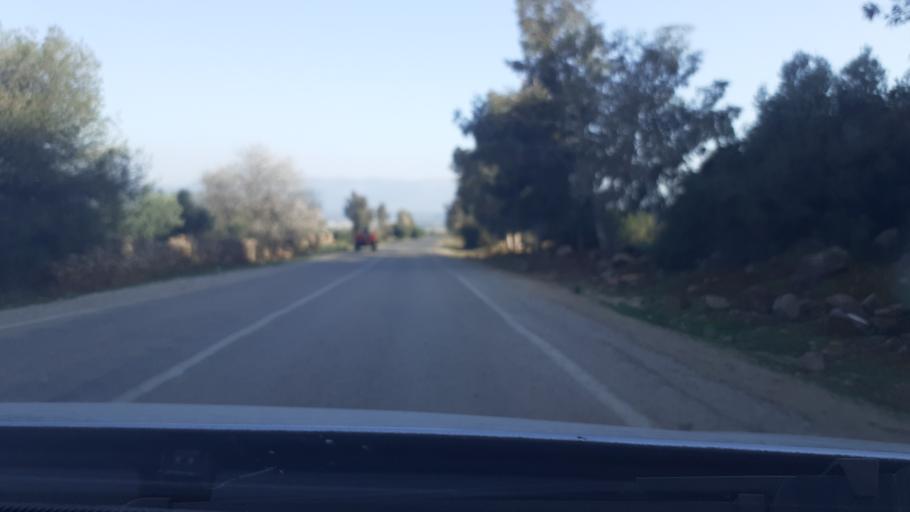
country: TR
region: Hatay
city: Aktepe
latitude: 36.7315
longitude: 36.4791
